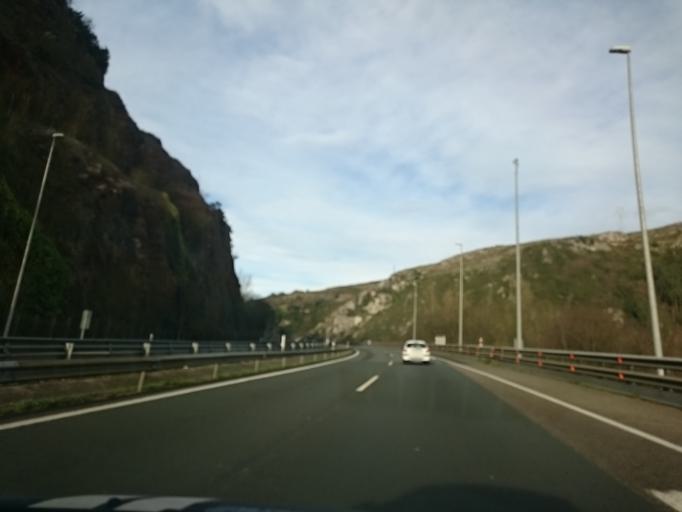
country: ES
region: Asturias
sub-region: Province of Asturias
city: Castandiello
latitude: 43.3001
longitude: -5.8460
